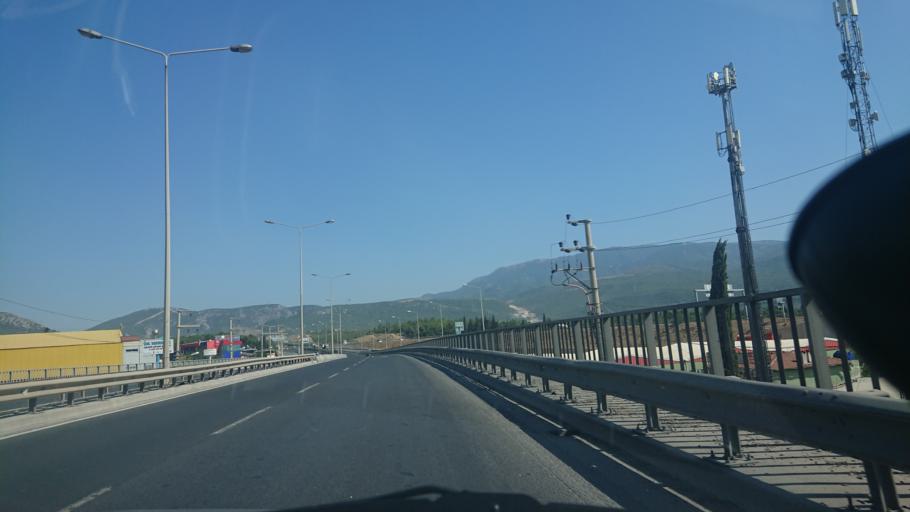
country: TR
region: Izmir
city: Bornova
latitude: 38.4522
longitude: 27.2662
